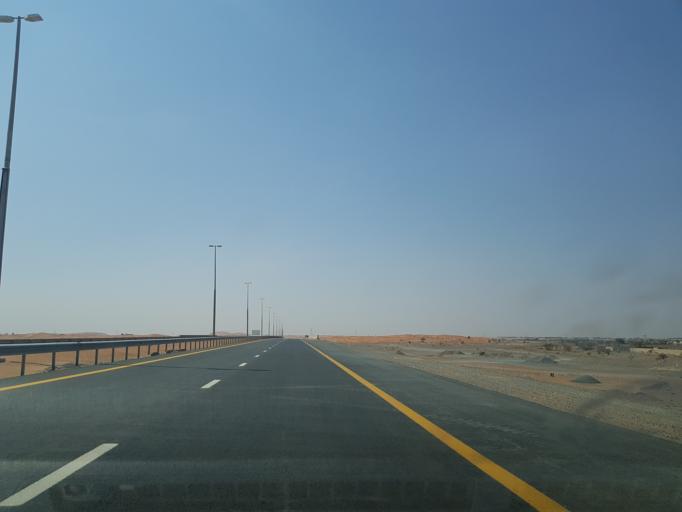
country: AE
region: Ash Shariqah
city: Adh Dhayd
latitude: 25.2385
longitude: 55.8922
